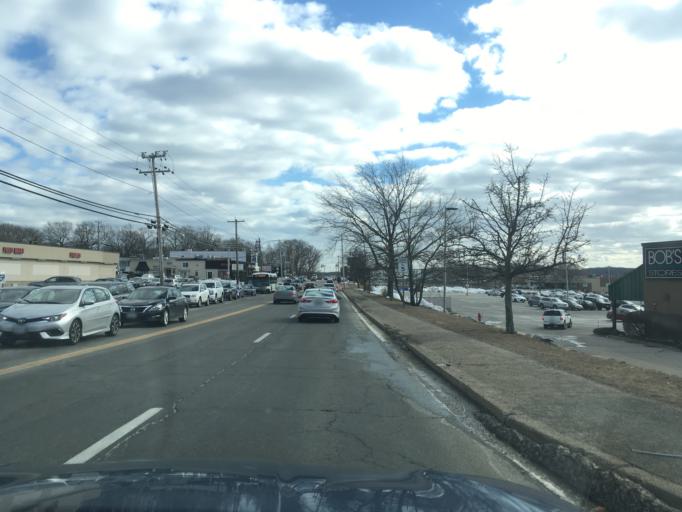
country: US
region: Rhode Island
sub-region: Kent County
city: West Warwick
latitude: 41.7340
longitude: -71.4775
